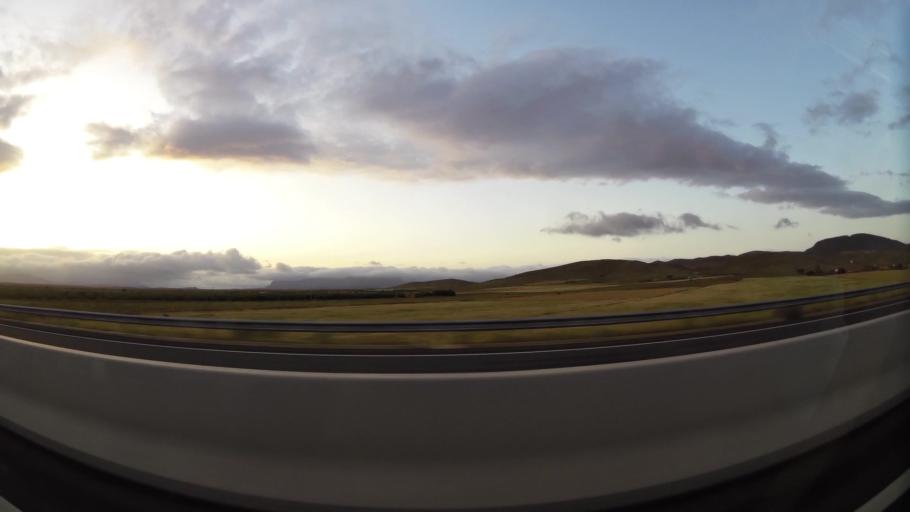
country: MA
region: Oriental
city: El Aioun
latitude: 34.5949
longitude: -2.6800
